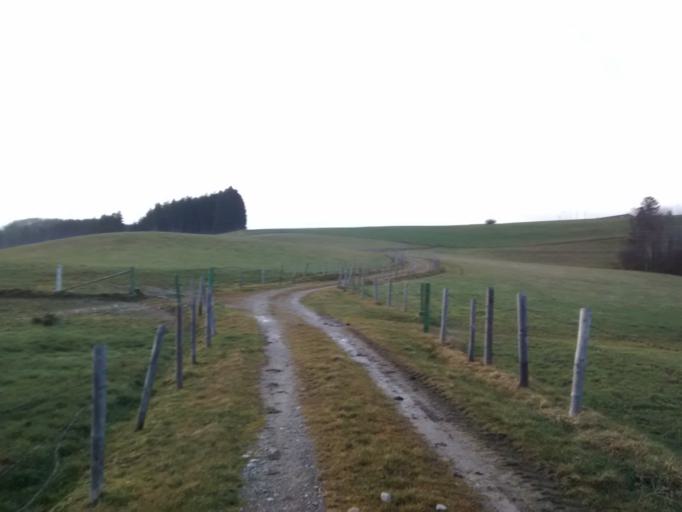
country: DE
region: Bavaria
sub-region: Swabia
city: Eggenthal
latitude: 47.8966
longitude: 10.4822
